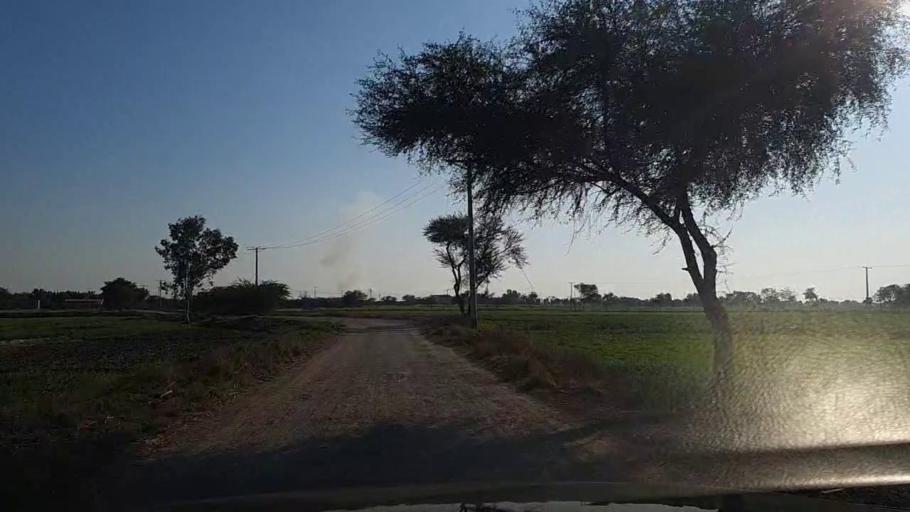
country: PK
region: Sindh
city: Nawabshah
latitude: 26.2072
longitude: 68.3749
